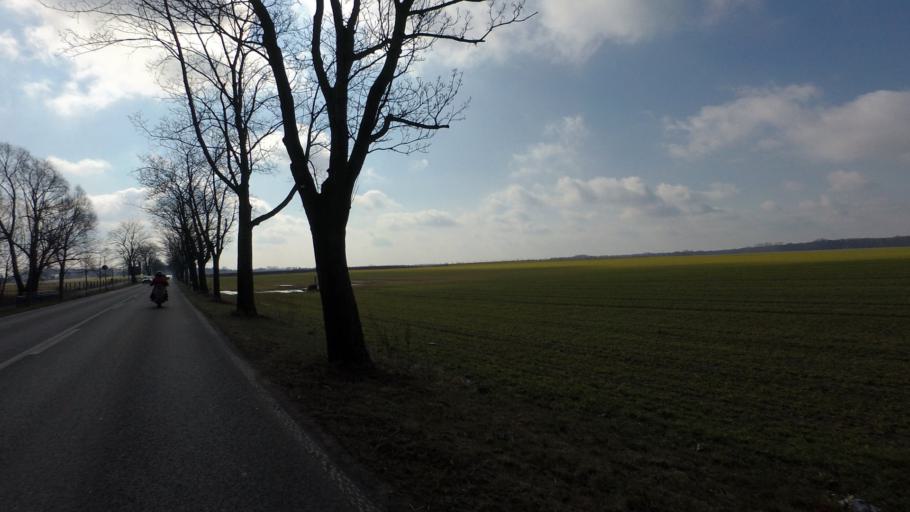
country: DE
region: Brandenburg
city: Glienicke
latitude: 52.6607
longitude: 13.3279
